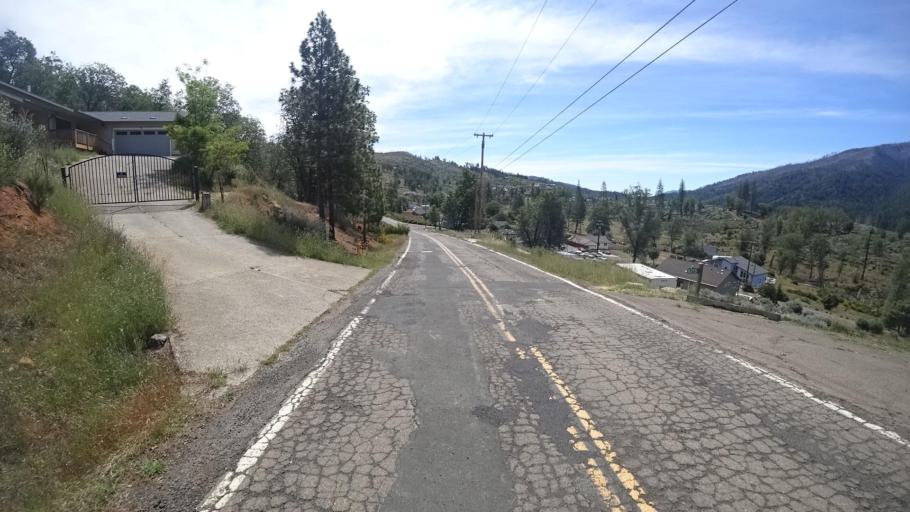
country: US
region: California
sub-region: Lake County
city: Cobb
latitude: 38.8457
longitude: -122.7359
